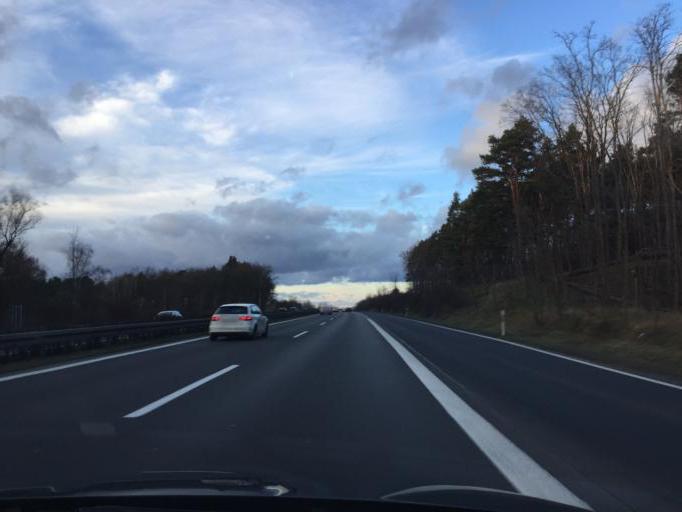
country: DE
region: Brandenburg
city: Mittenwalde
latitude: 52.2672
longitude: 13.5758
